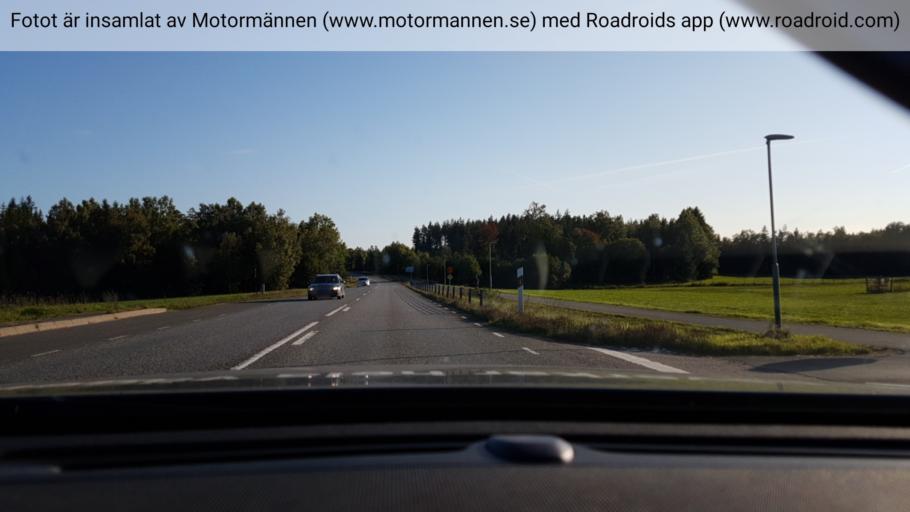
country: SE
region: Joenkoeping
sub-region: Gislaveds Kommun
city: Smalandsstenar
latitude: 57.1344
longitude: 13.3811
